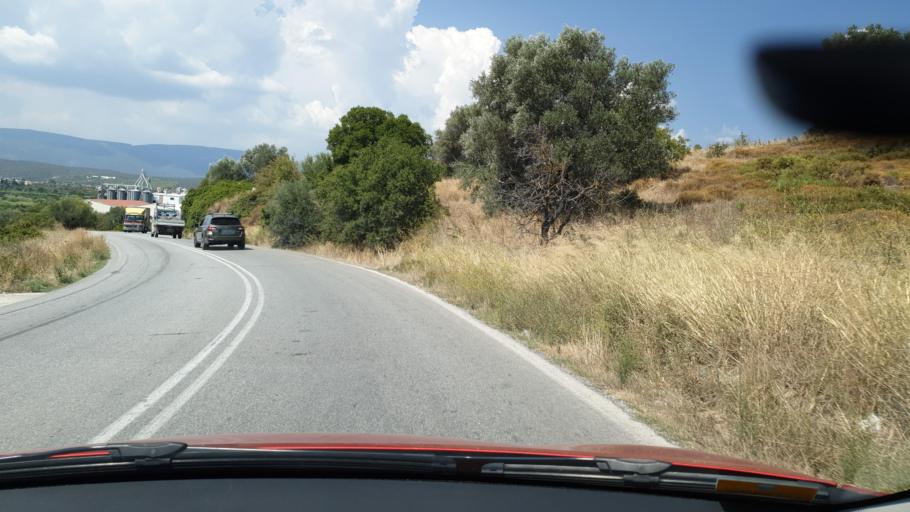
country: GR
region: Central Greece
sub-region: Nomos Evvoias
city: Aliveri
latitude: 38.3971
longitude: 24.0644
